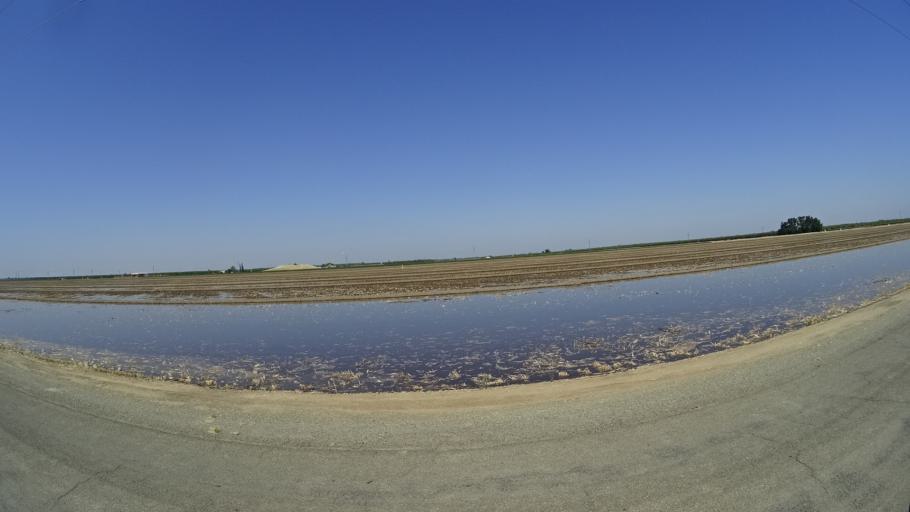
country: US
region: California
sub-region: Kings County
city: Lucerne
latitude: 36.4051
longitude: -119.5828
